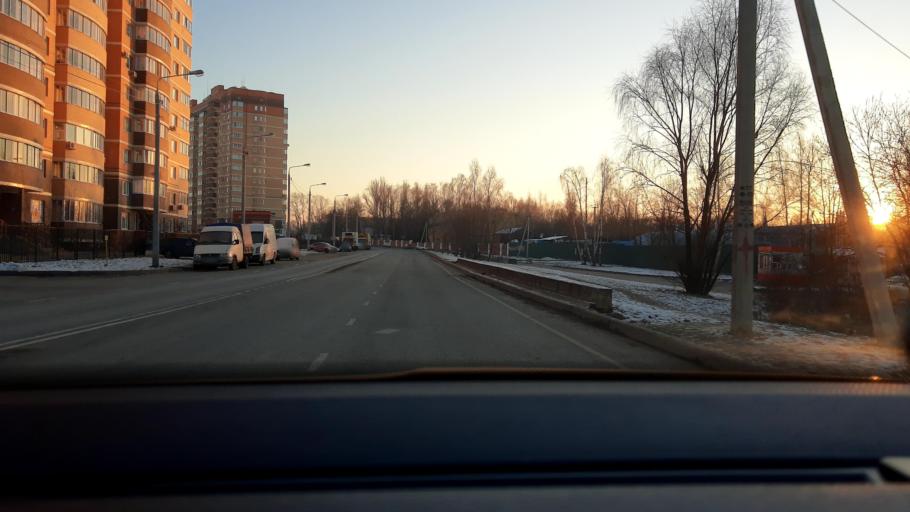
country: RU
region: Moskovskaya
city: Dolgoprudnyy
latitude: 55.9623
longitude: 37.5196
